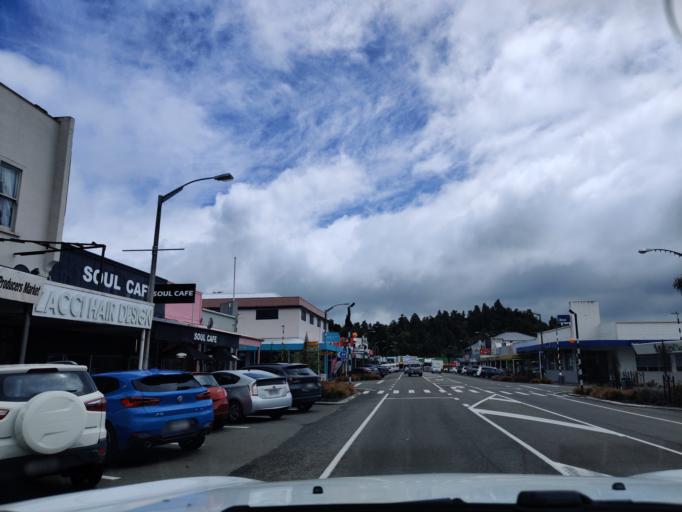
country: NZ
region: Manawatu-Wanganui
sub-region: Ruapehu District
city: Waiouru
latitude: -39.6783
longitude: 175.7992
